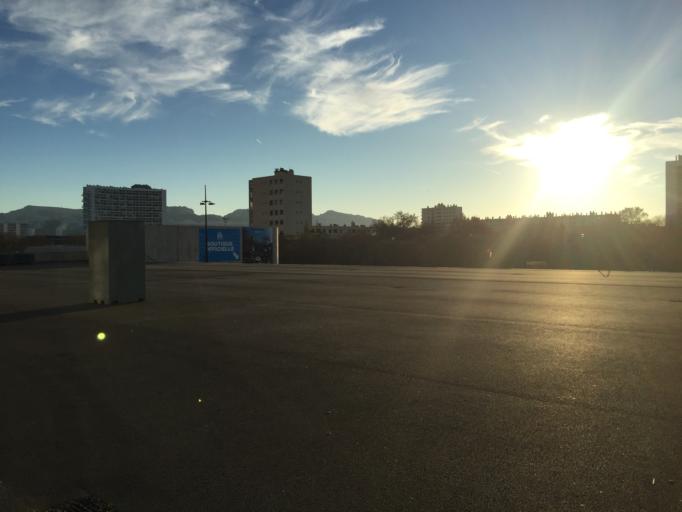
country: FR
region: Provence-Alpes-Cote d'Azur
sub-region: Departement des Bouches-du-Rhone
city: Marseille 08
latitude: 43.2695
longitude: 5.3943
